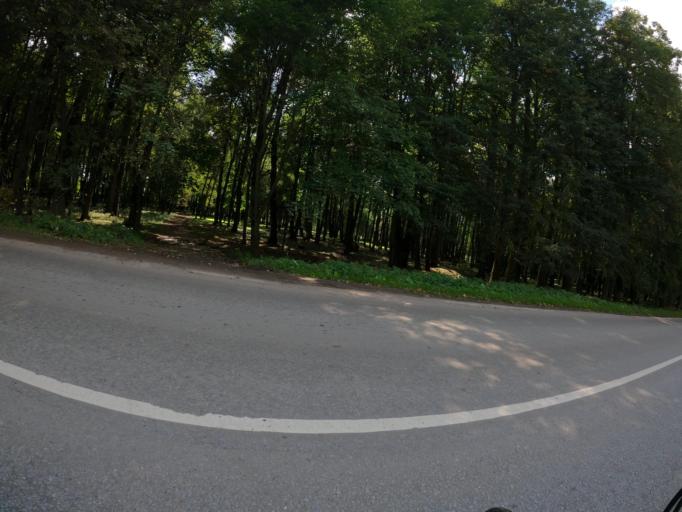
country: RU
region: Moskovskaya
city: Voskresensk
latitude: 55.2753
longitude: 38.6519
